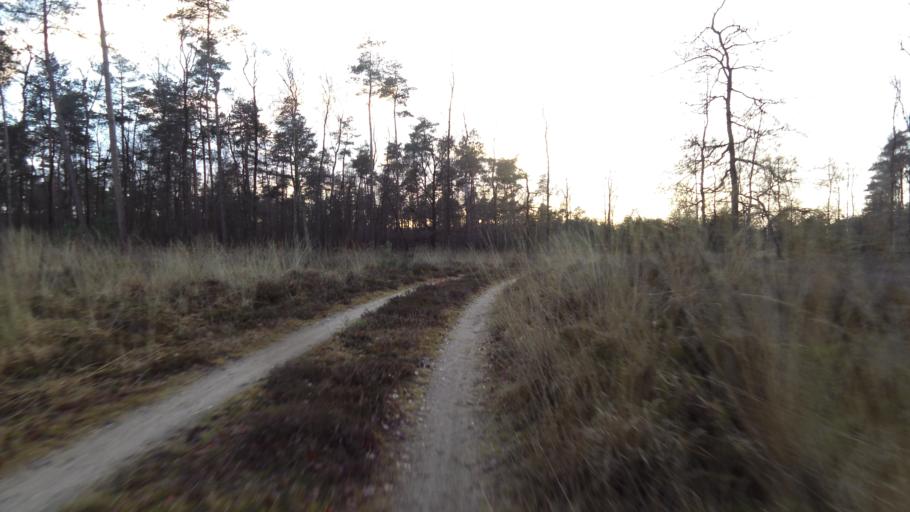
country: NL
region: Gelderland
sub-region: Gemeente Apeldoorn
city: Uddel
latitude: 52.3052
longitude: 5.8532
